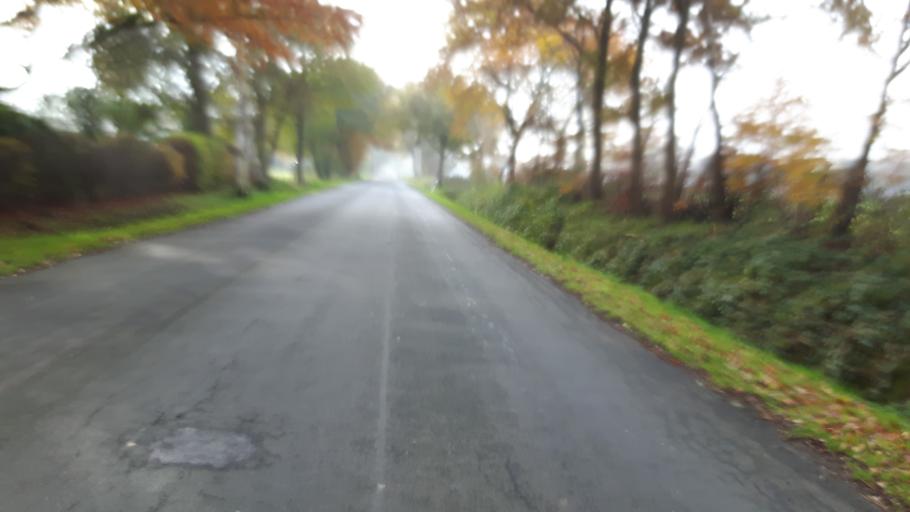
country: DE
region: Lower Saxony
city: Delmenhorst
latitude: 53.0271
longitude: 8.5925
